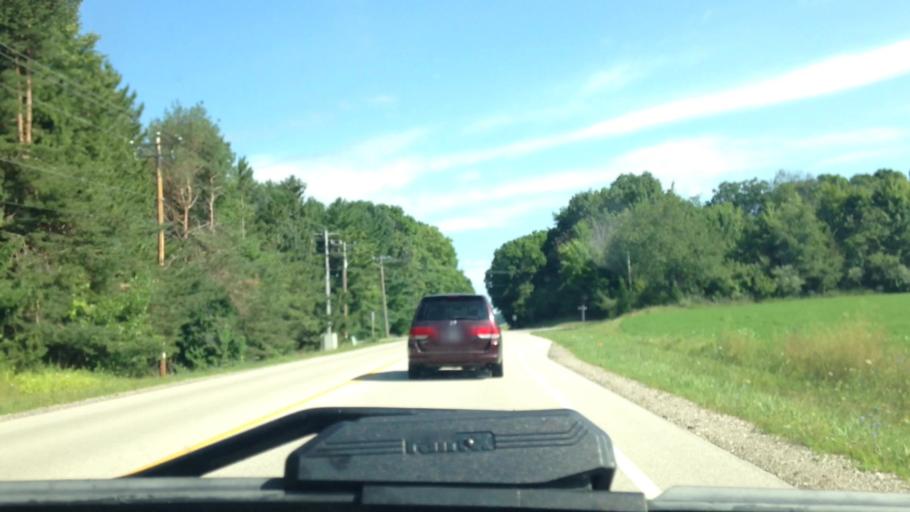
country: US
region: Wisconsin
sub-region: Washington County
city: West Bend
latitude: 43.3972
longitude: -88.2409
